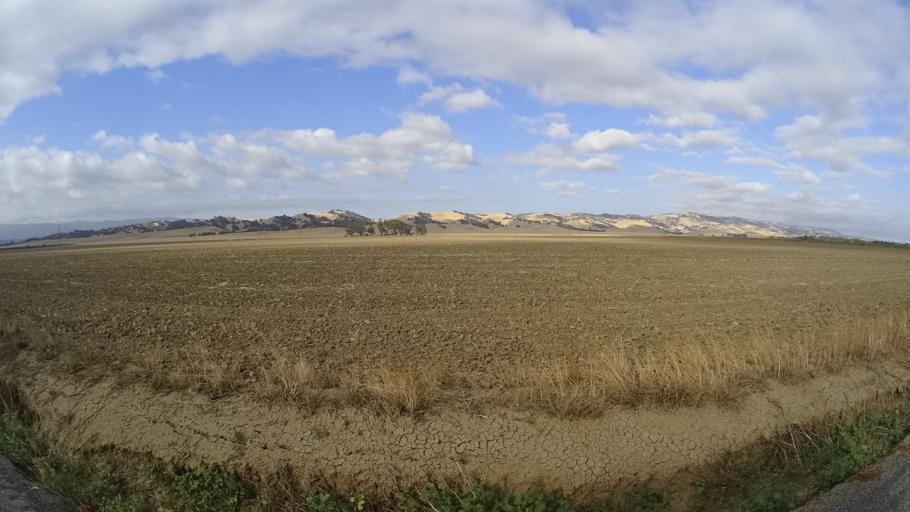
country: US
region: California
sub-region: Yolo County
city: Esparto
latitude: 38.7463
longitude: -122.0448
